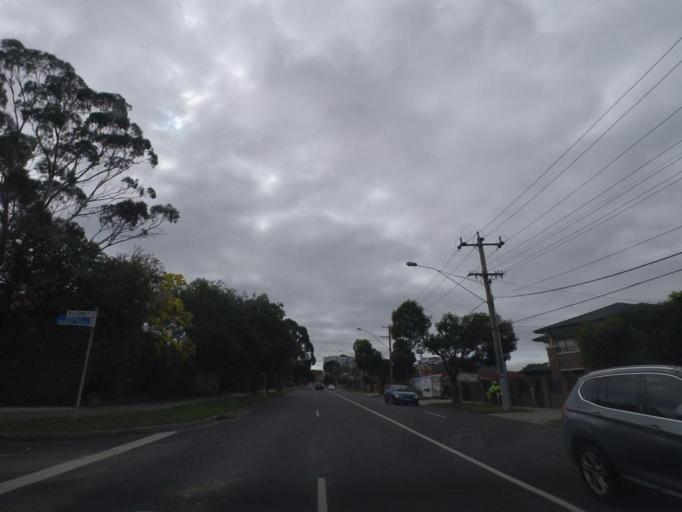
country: AU
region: Victoria
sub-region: Manningham
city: Doncaster
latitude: -37.7924
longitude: 145.1217
